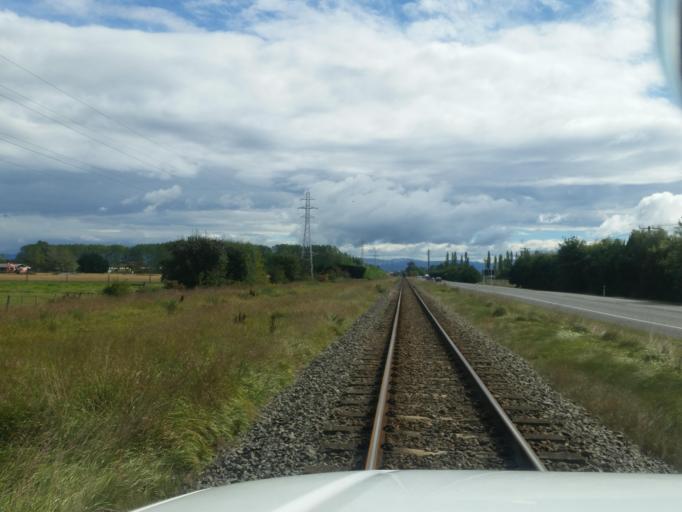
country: NZ
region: Canterbury
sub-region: Waimakariri District
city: Kaiapoi
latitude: -43.3380
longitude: 172.6105
